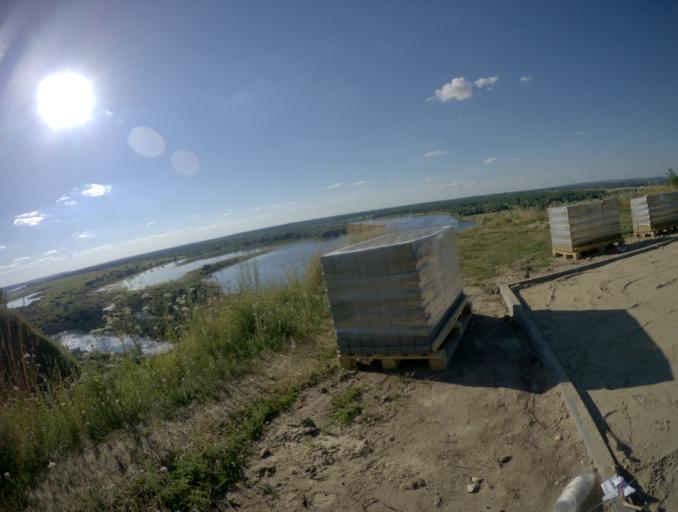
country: RU
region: Nizjnij Novgorod
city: Taremskoye
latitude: 55.9608
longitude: 43.0474
